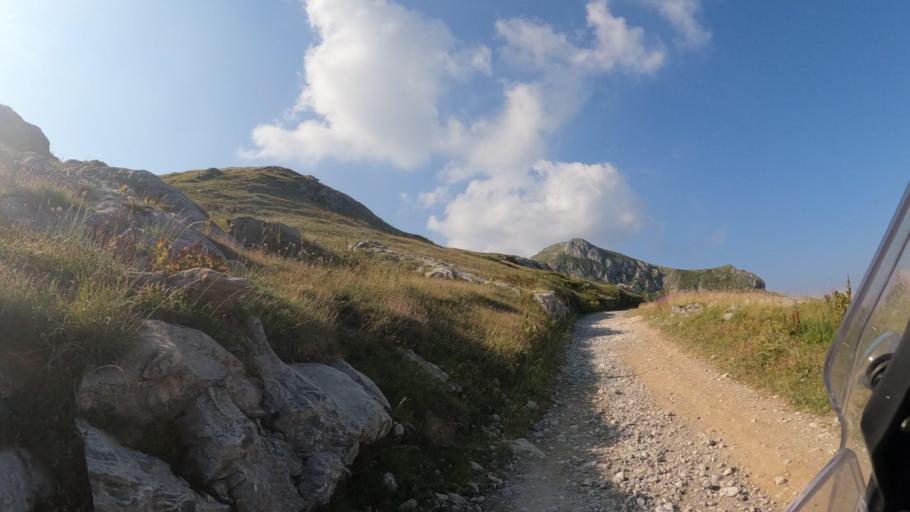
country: IT
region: Piedmont
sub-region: Provincia di Cuneo
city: Limone Piemonte
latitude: 44.1609
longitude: 7.6701
